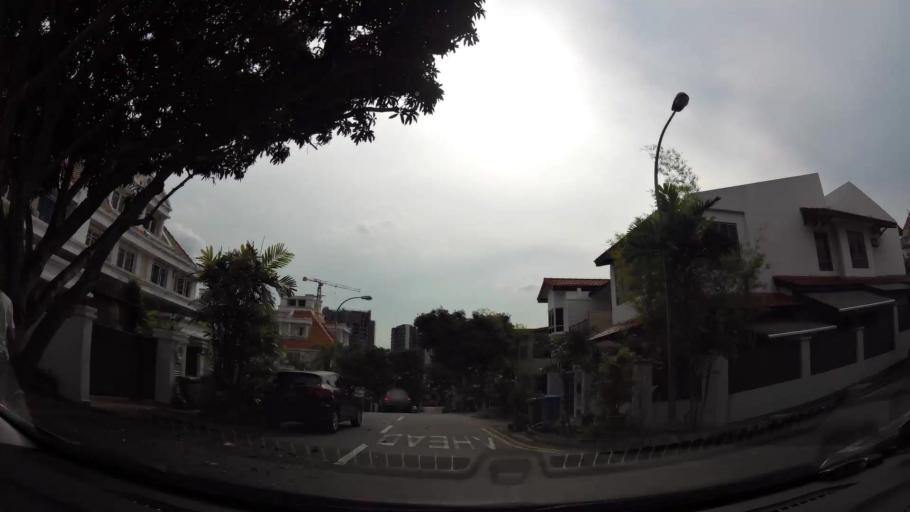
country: SG
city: Singapore
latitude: 1.3452
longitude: 103.8845
